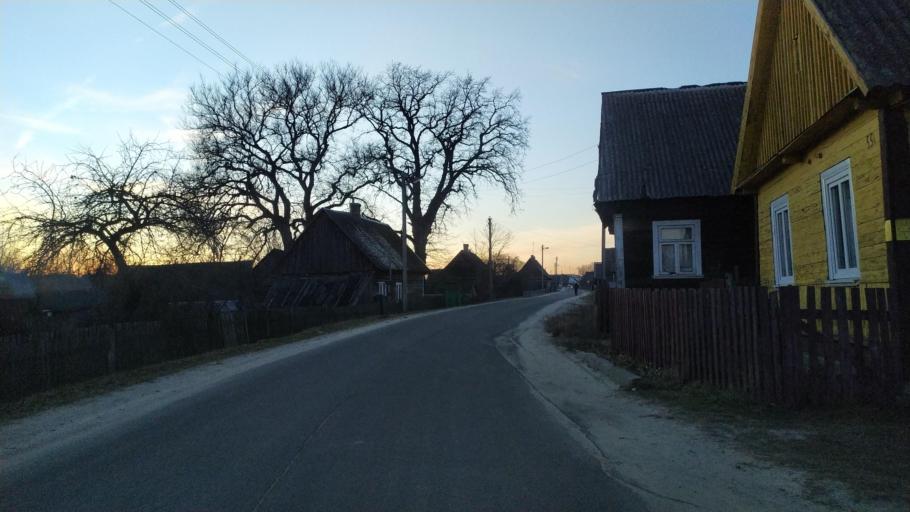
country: BY
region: Brest
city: Pruzhany
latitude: 52.5535
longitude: 24.2226
